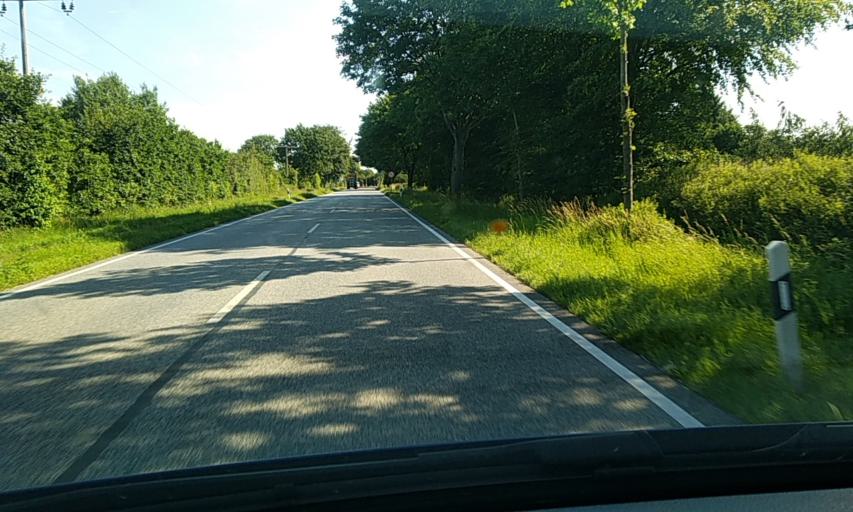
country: DE
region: Schleswig-Holstein
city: Fockbek
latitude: 54.2956
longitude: 9.5876
